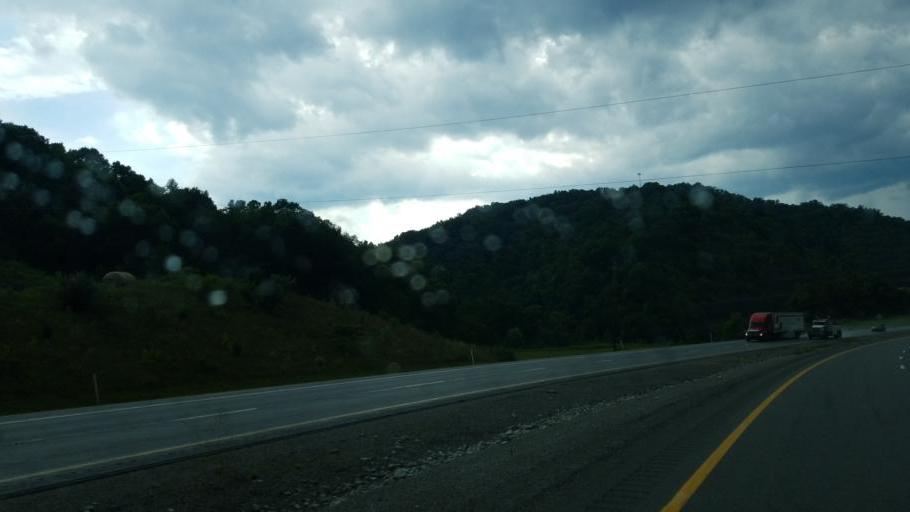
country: US
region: Kentucky
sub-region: Pike County
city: Pikeville
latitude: 37.5130
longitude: -82.4698
